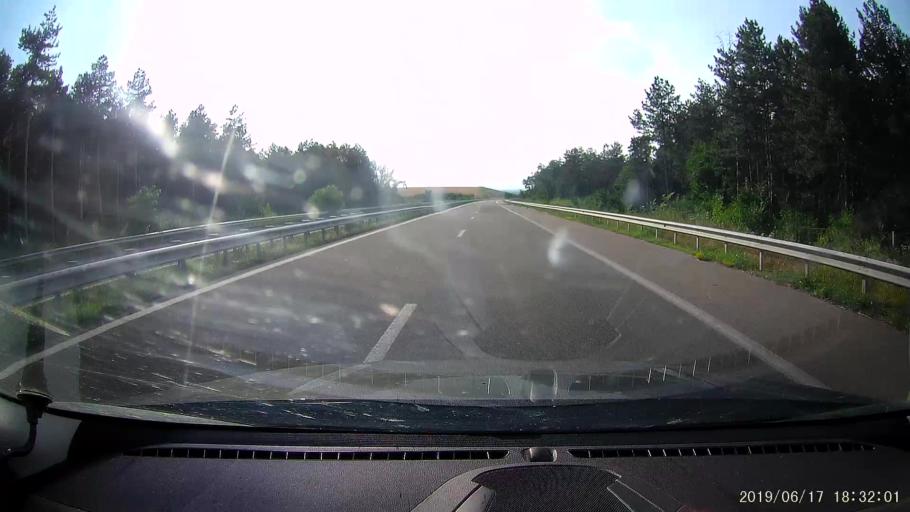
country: BG
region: Khaskovo
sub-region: Obshtina Dimitrovgrad
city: Dimitrovgrad
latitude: 42.0536
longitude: 25.4893
